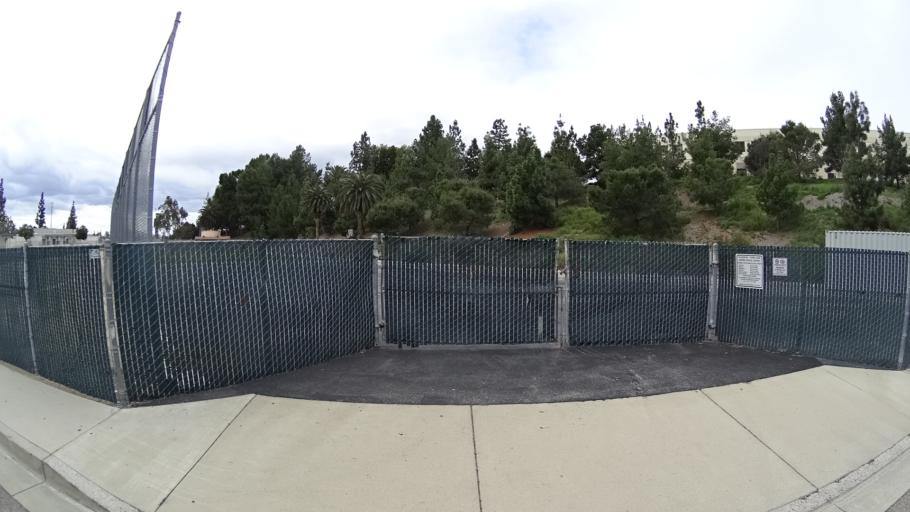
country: US
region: California
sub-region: Orange County
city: Yorba Linda
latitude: 33.8697
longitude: -117.8372
